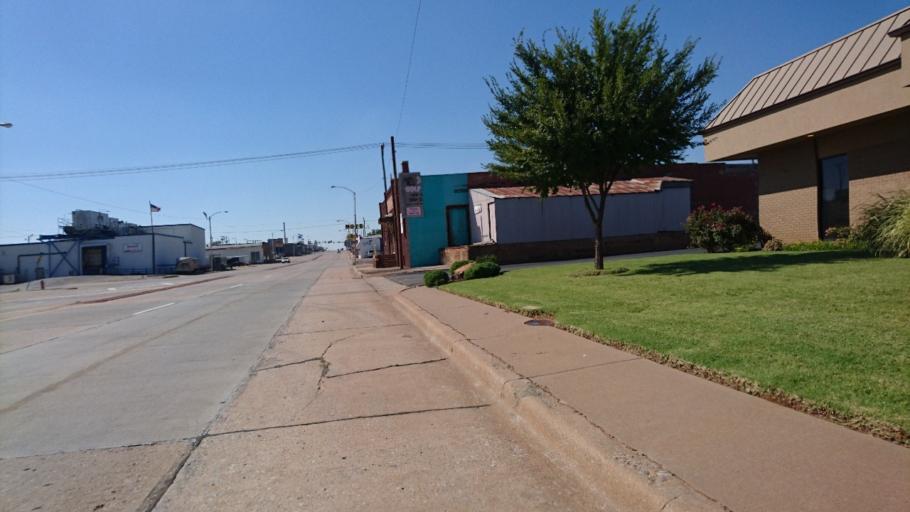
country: US
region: Oklahoma
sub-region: Custer County
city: Clinton
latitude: 35.5155
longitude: -98.9604
